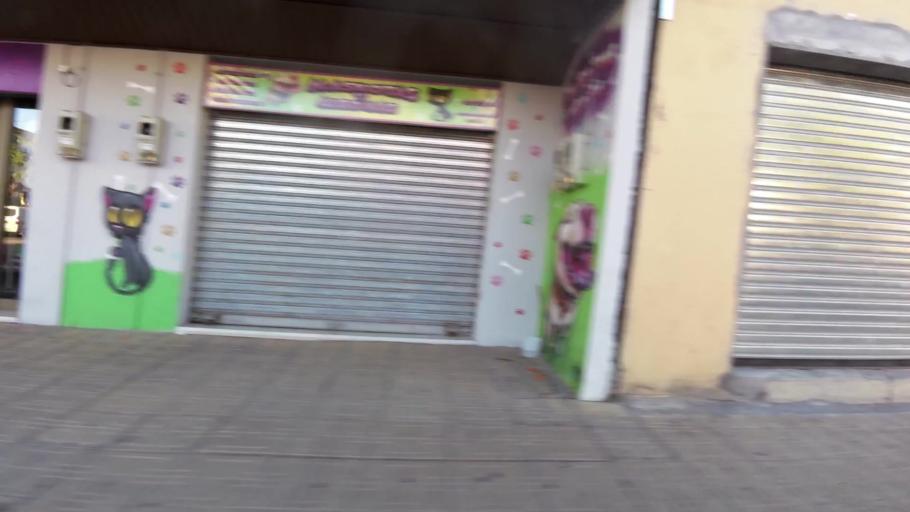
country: CL
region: Maule
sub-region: Provincia de Curico
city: Curico
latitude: -34.9860
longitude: -71.2428
